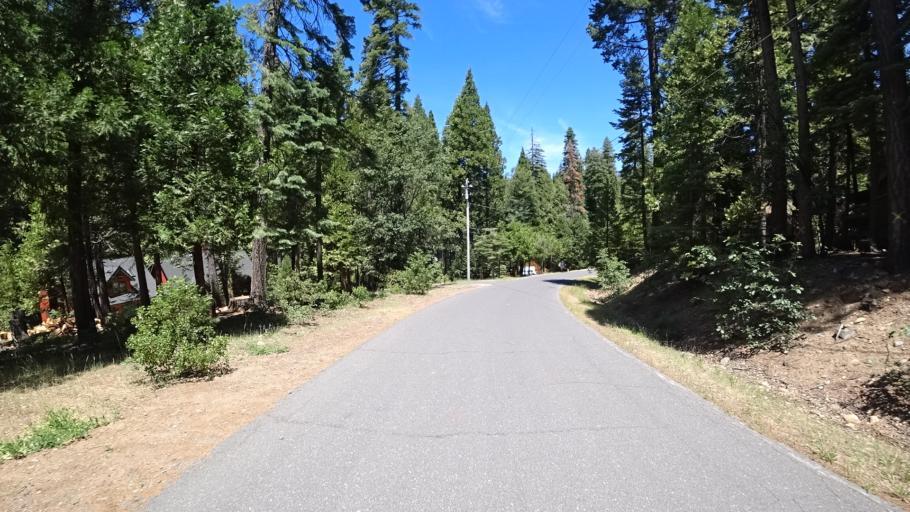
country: US
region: California
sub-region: Calaveras County
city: Arnold
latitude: 38.3169
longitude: -120.2594
